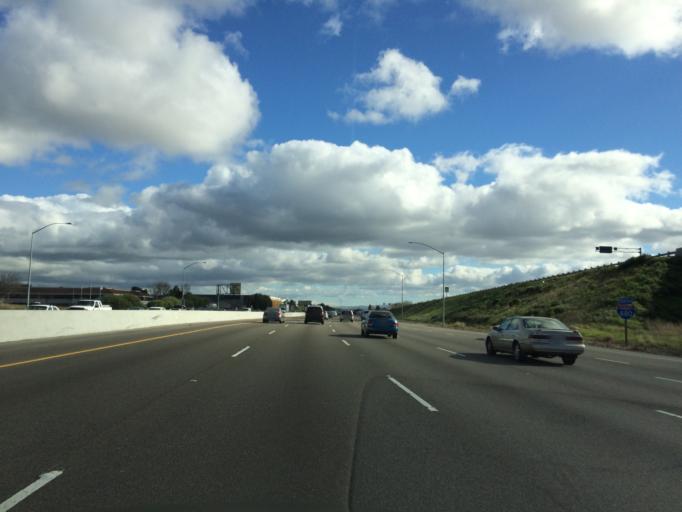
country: US
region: California
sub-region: Santa Clara County
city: Milpitas
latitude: 37.4820
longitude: -121.9357
